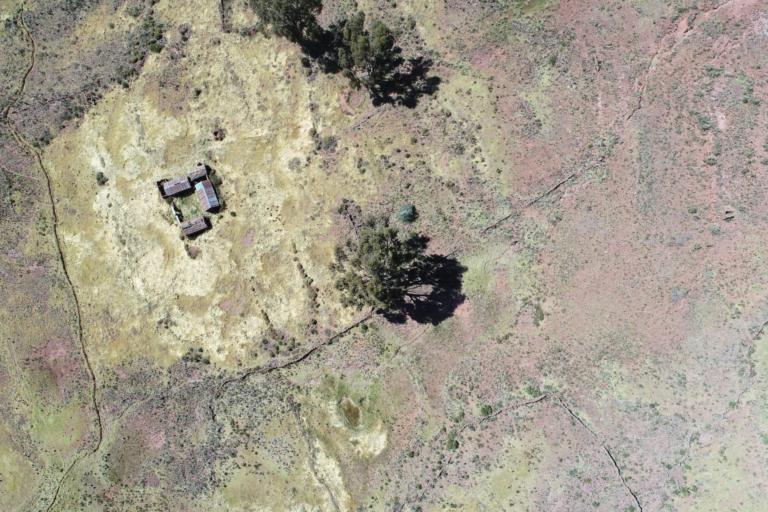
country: BO
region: La Paz
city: Tiahuanaco
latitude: -16.6075
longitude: -68.7695
